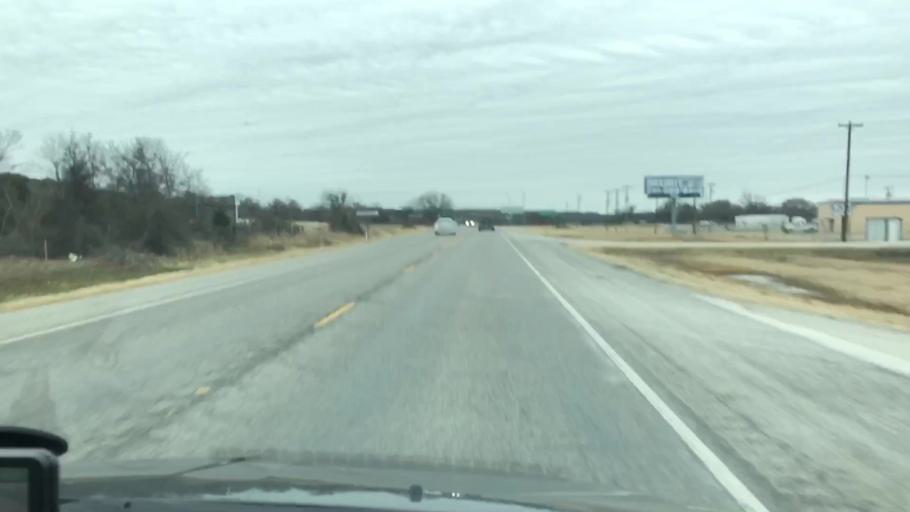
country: US
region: Texas
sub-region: Palo Pinto County
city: Mineral Wells
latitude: 32.8522
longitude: -98.0960
